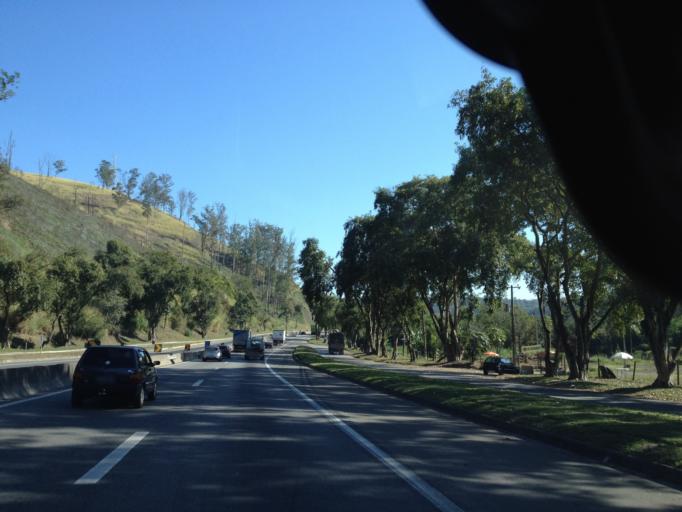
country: BR
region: Rio de Janeiro
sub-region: Barra Mansa
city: Barra Mansa
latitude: -22.4942
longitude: -44.2410
